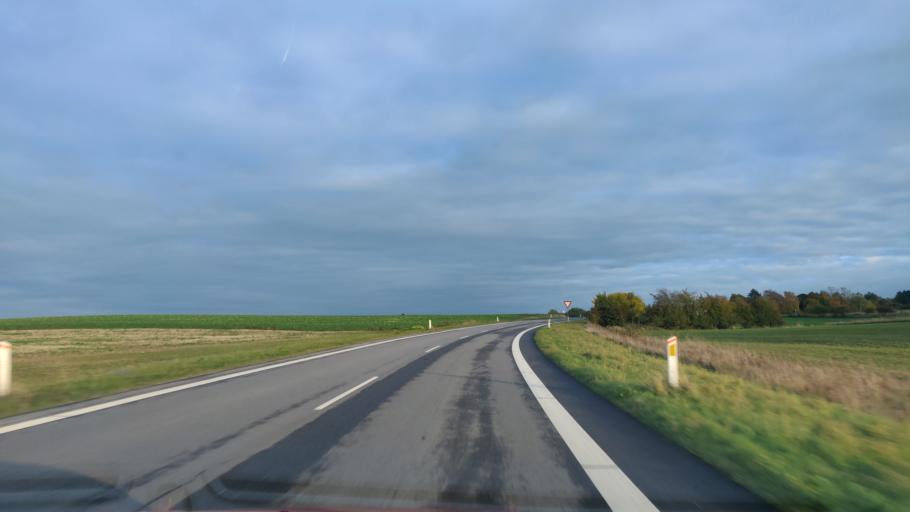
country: DK
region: Zealand
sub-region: Holbaek Kommune
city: Vipperod
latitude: 55.6836
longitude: 11.7304
